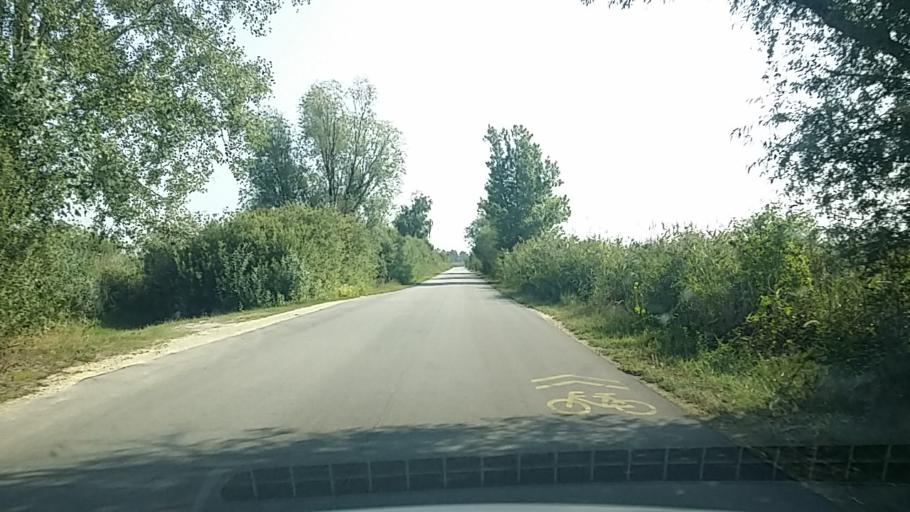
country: HU
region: Gyor-Moson-Sopron
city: Fertorakos
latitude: 47.7178
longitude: 16.6763
